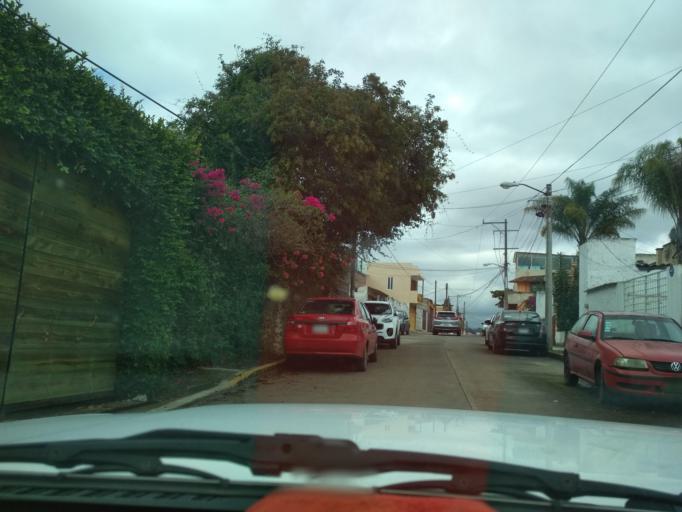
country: MX
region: Veracruz
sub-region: Xalapa
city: Xalapa de Enriquez
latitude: 19.5064
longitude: -96.9257
